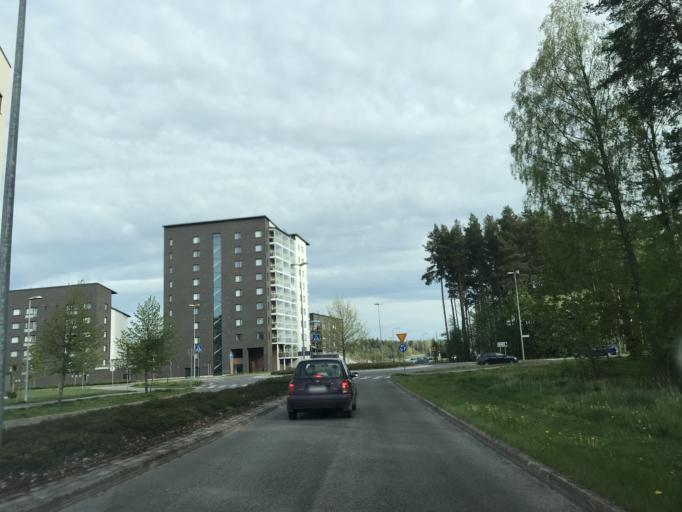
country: FI
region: Varsinais-Suomi
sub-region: Turku
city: Kaarina
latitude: 60.4281
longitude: 22.3202
